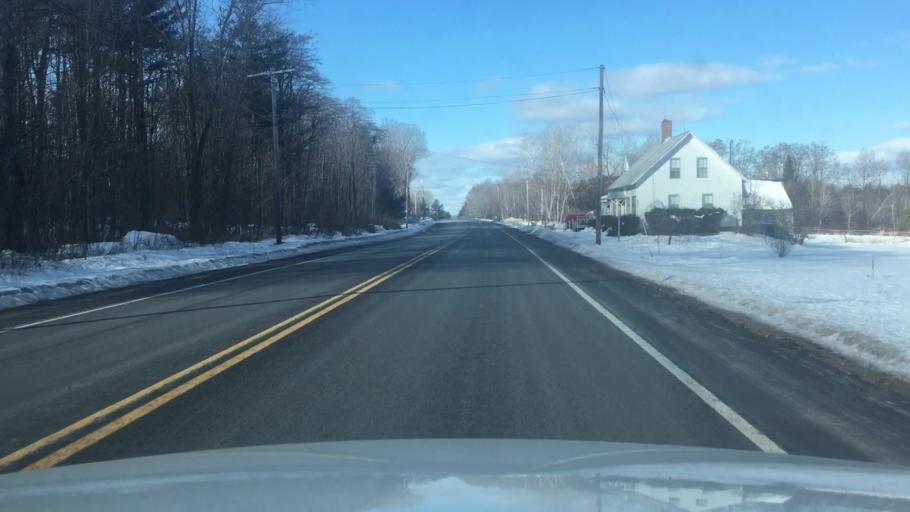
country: US
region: Maine
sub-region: Somerset County
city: Skowhegan
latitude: 44.8180
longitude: -69.7696
